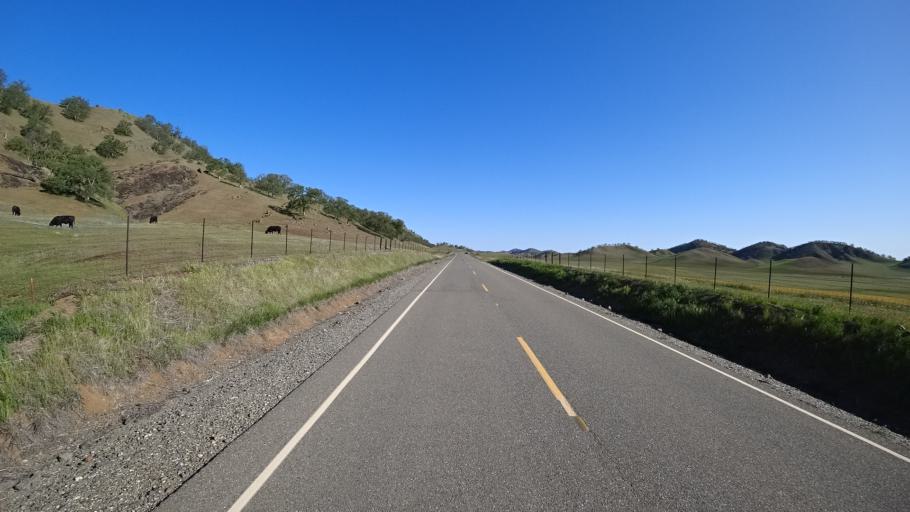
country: US
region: California
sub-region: Tehama County
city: Rancho Tehama Reserve
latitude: 39.7590
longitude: -122.5246
